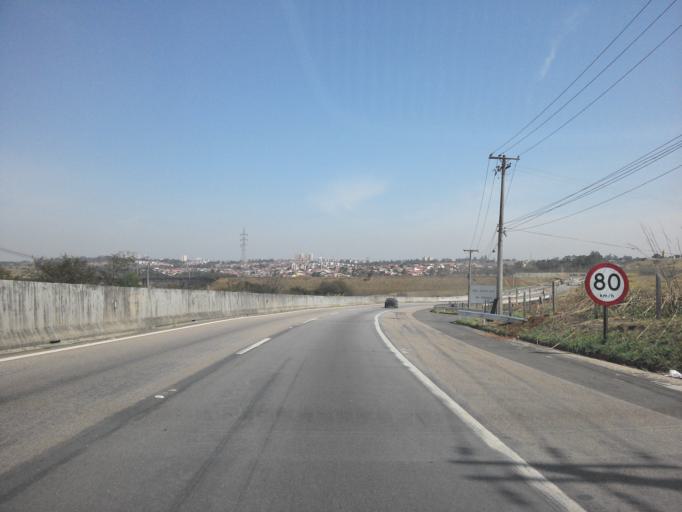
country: BR
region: Sao Paulo
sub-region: Campinas
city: Campinas
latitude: -22.8936
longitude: -47.1322
